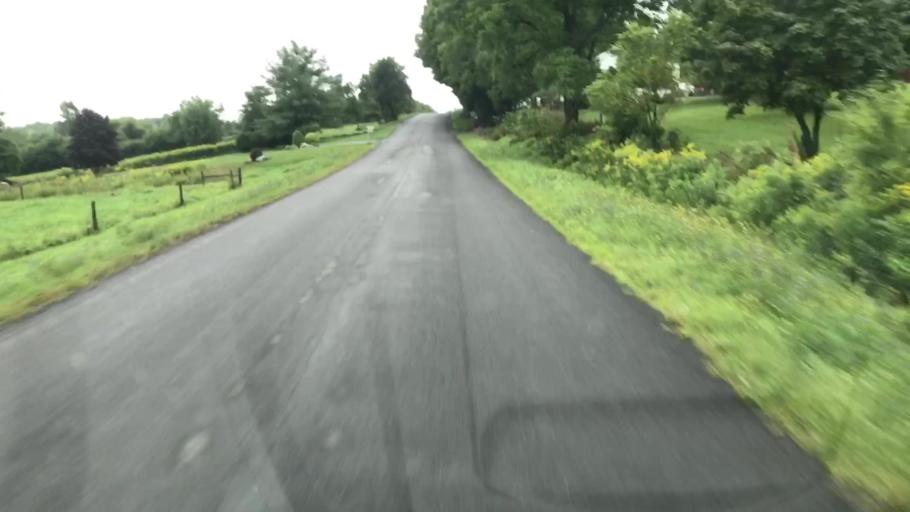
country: US
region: New York
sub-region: Cayuga County
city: Melrose Park
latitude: 42.9322
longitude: -76.5087
